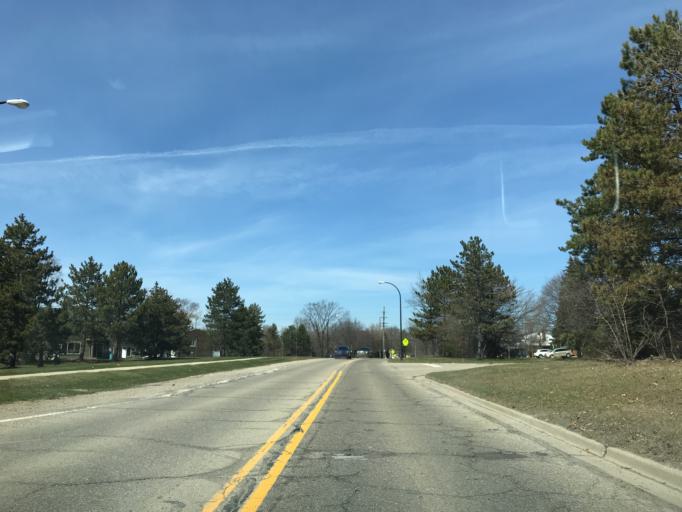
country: US
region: Michigan
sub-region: Washtenaw County
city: Ann Arbor
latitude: 42.3080
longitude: -83.7077
